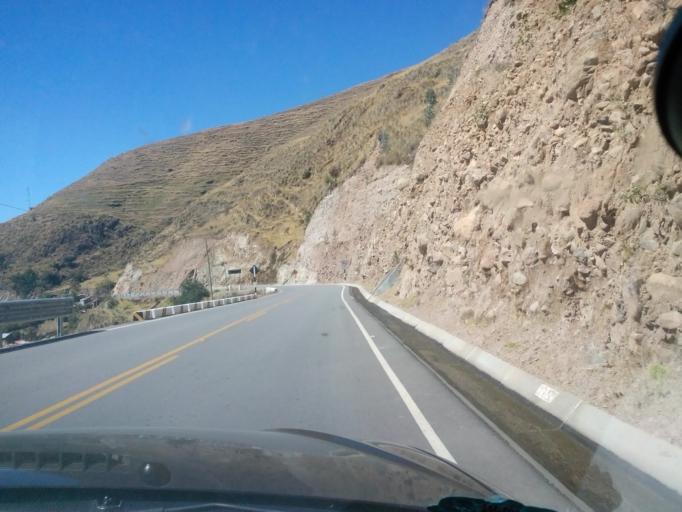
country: PE
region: Ayacucho
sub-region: Provincia de Huamanga
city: Ocros
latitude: -13.3911
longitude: -73.9262
